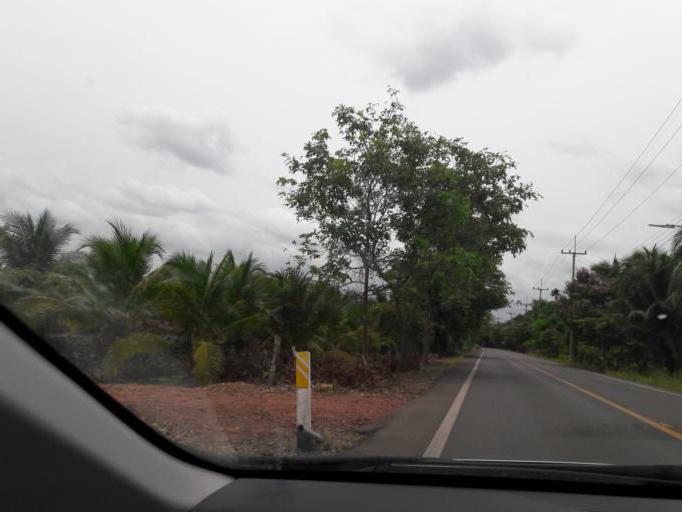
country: TH
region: Samut Sakhon
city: Ban Phaeo
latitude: 13.6151
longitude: 100.0226
